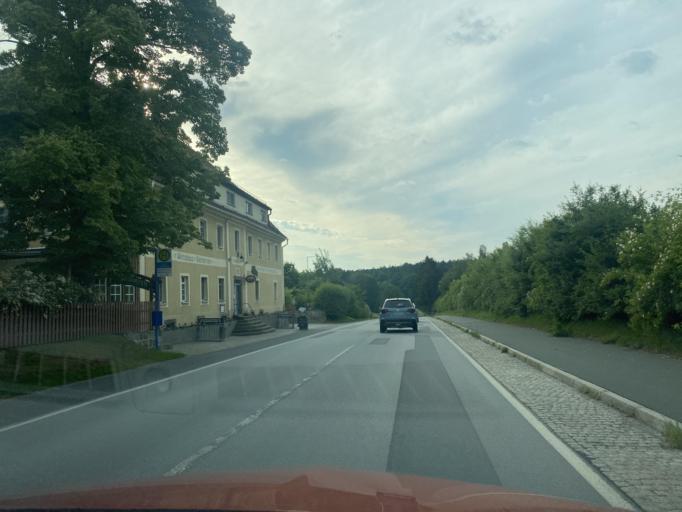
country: DE
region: Saxony
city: Herrnhut
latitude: 51.0014
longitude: 14.7657
